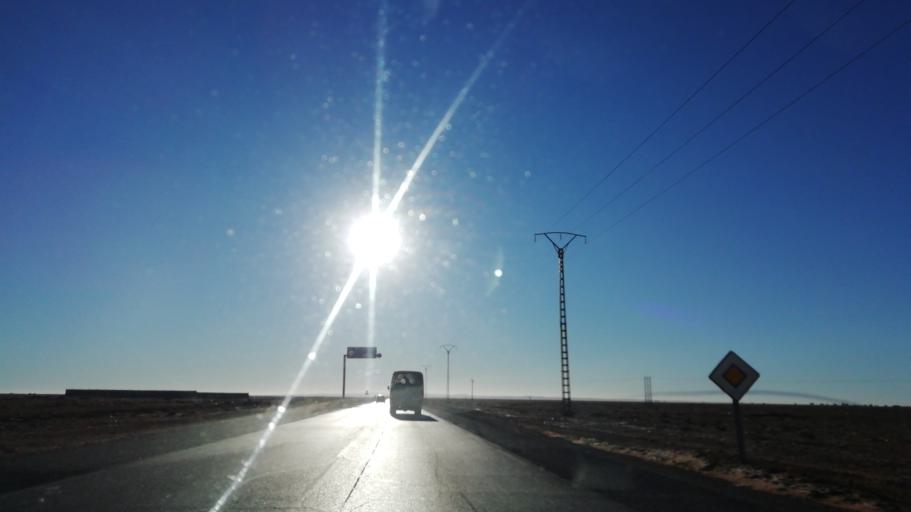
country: DZ
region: Saida
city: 'Ain el Hadjar
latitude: 34.0209
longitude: 0.1039
